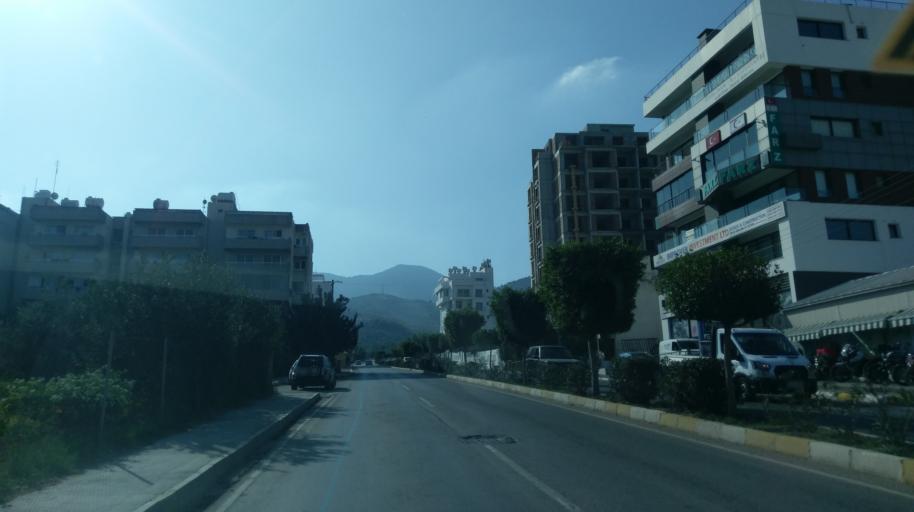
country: CY
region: Keryneia
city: Kyrenia
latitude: 35.3294
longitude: 33.3192
